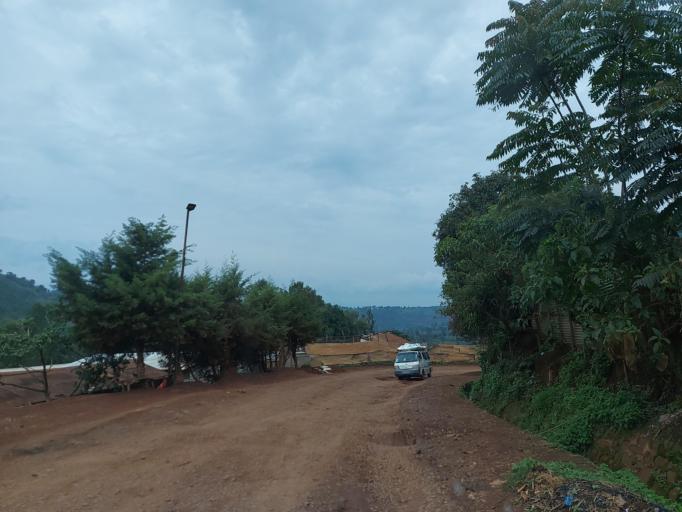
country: CD
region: South Kivu
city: Bukavu
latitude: -2.4749
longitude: 28.8226
